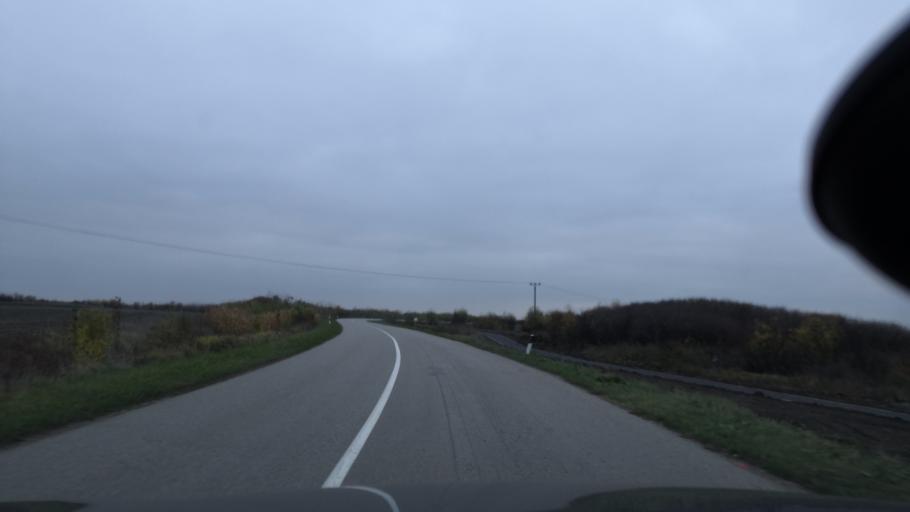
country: RS
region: Autonomna Pokrajina Vojvodina
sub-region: Severnobanatski Okrug
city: Novi Knezevac
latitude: 46.1057
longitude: 20.1038
